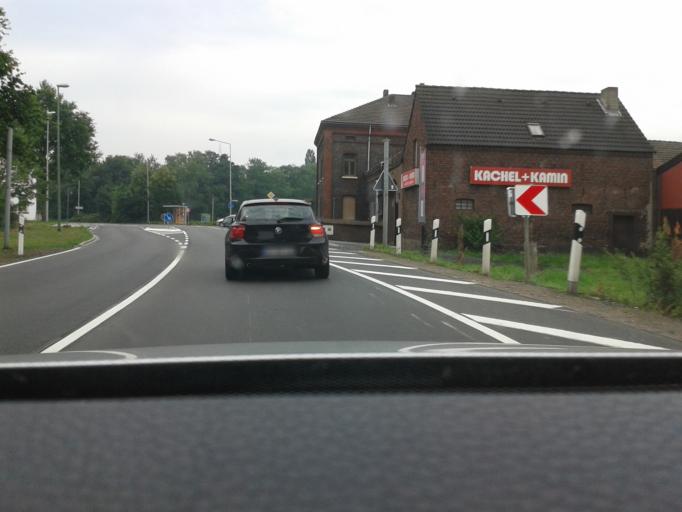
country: DE
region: North Rhine-Westphalia
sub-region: Regierungsbezirk Dusseldorf
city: Hochfeld
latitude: 51.4251
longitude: 6.6990
